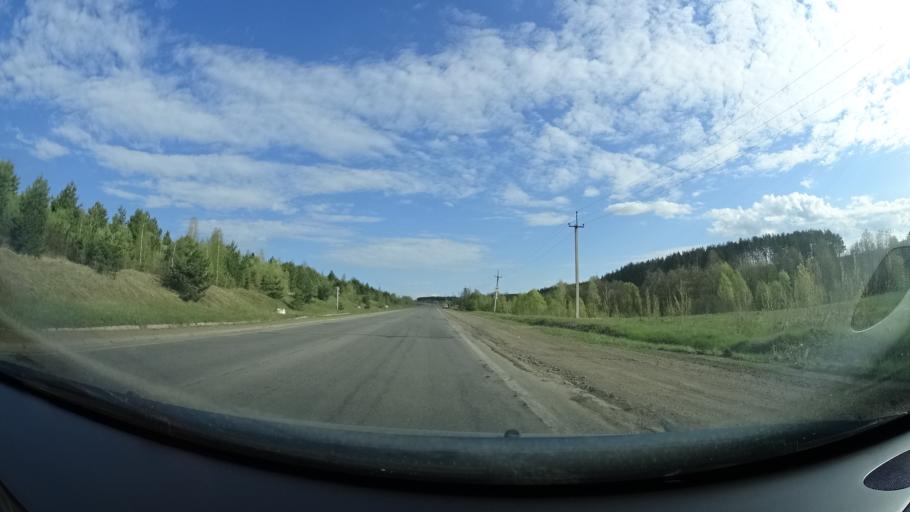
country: RU
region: Bashkortostan
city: Blagoveshchensk
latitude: 55.0746
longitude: 55.8076
